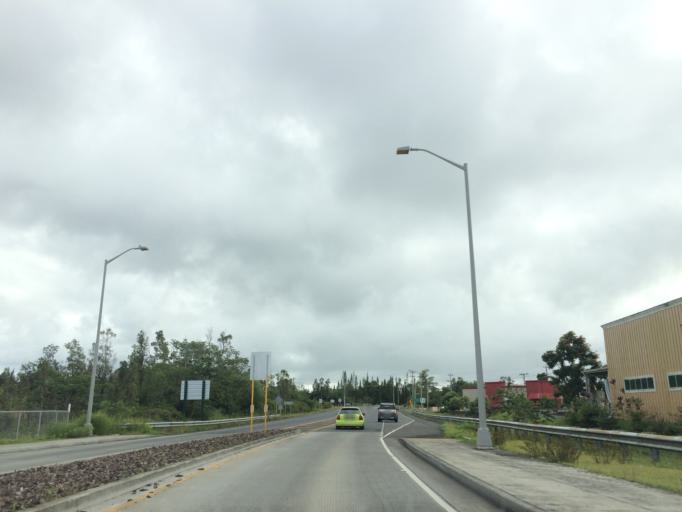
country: US
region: Hawaii
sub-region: Hawaii County
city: Hawaiian Paradise Park
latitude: 19.5052
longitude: -154.9556
